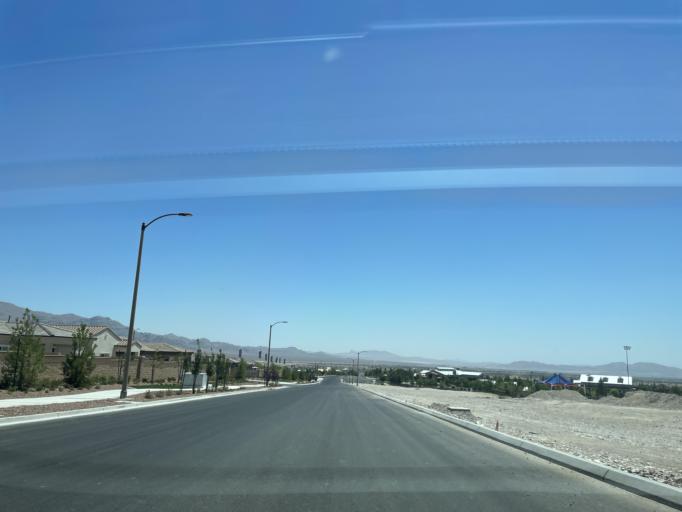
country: US
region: Nevada
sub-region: Clark County
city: Summerlin South
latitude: 36.3141
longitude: -115.3192
